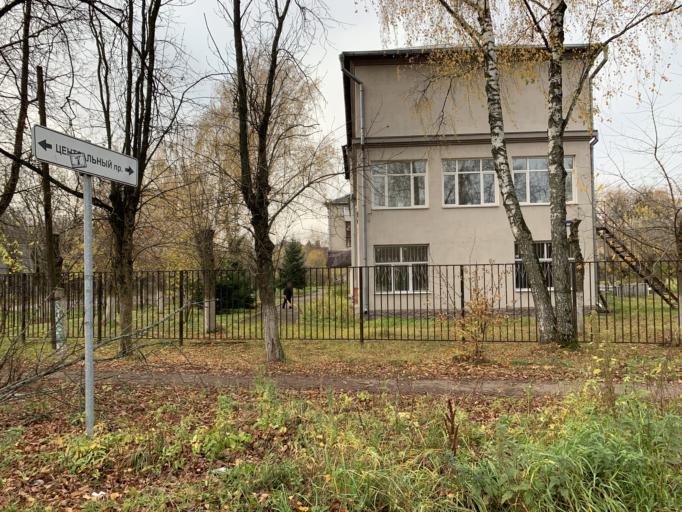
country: RU
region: Moskovskaya
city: Lesnyye Polyany
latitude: 55.9881
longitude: 37.8505
